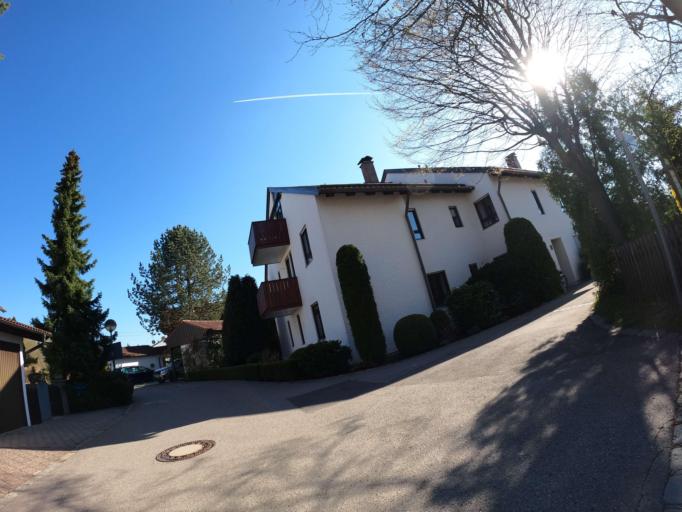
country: DE
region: Bavaria
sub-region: Upper Bavaria
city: Ottobrunn
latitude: 48.0735
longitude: 11.6731
